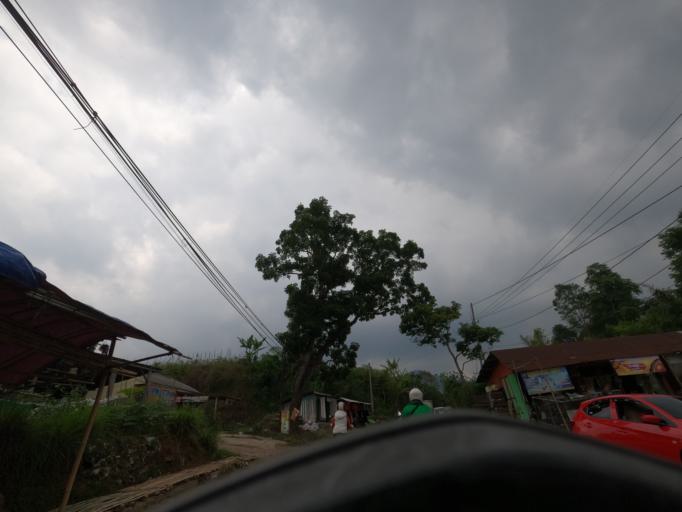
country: ID
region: West Java
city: Sukabumi
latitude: -6.7797
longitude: 107.0628
